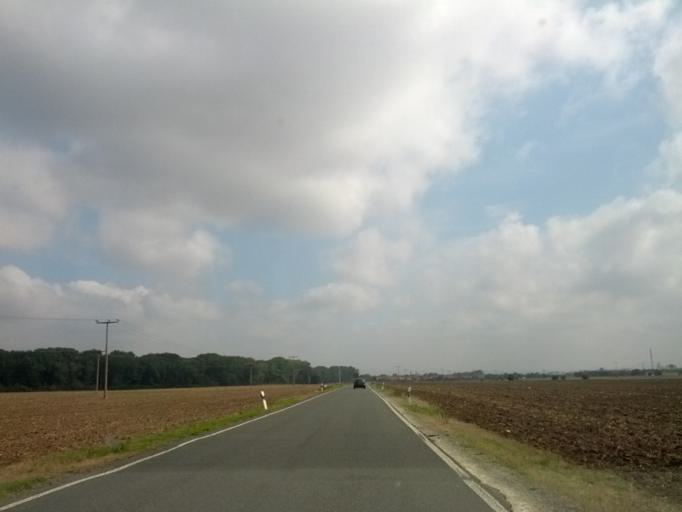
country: DE
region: Thuringia
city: Seebergen
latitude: 50.9017
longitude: 10.8203
